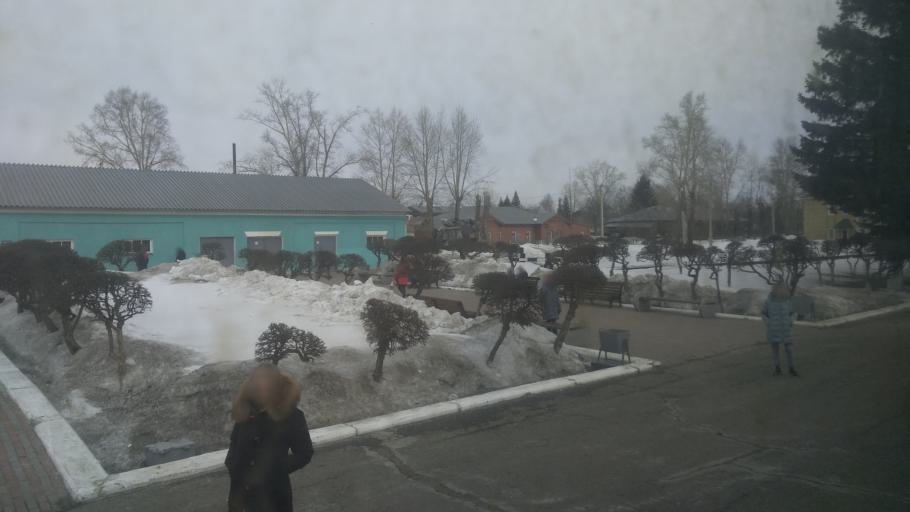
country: RU
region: Novosibirsk
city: Bolotnoye
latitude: 55.6681
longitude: 84.3948
